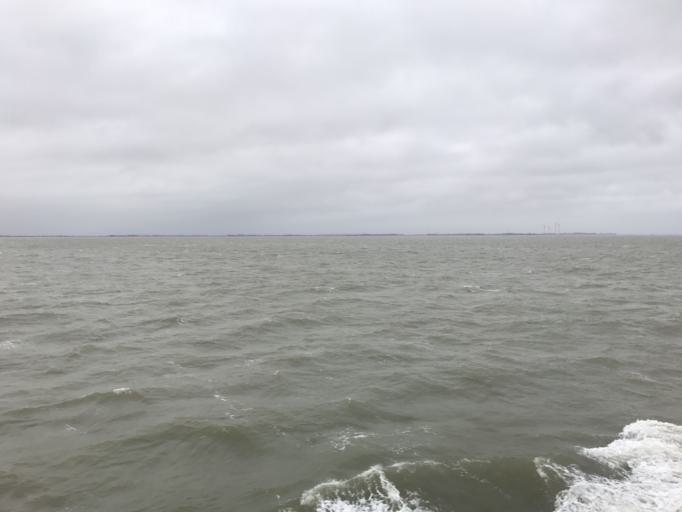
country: NL
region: Groningen
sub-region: Gemeente Delfzijl
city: Delfzijl
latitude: 53.4036
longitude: 6.9472
